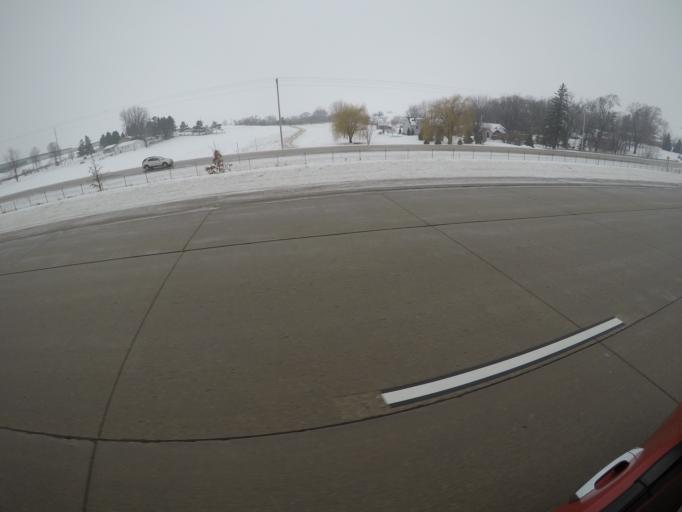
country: US
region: Minnesota
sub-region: Olmsted County
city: Oronoco
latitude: 44.1027
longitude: -92.5136
